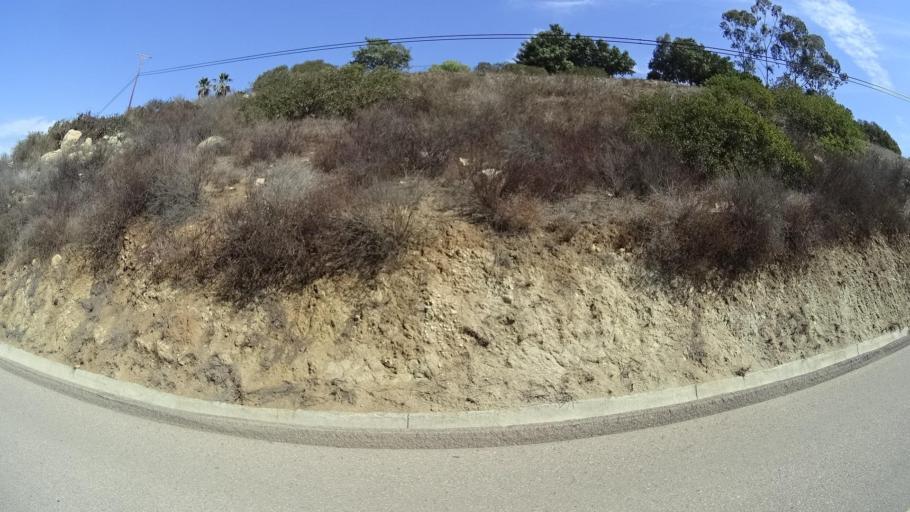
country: US
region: California
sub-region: San Diego County
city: Rancho San Diego
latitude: 32.7188
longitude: -116.9282
